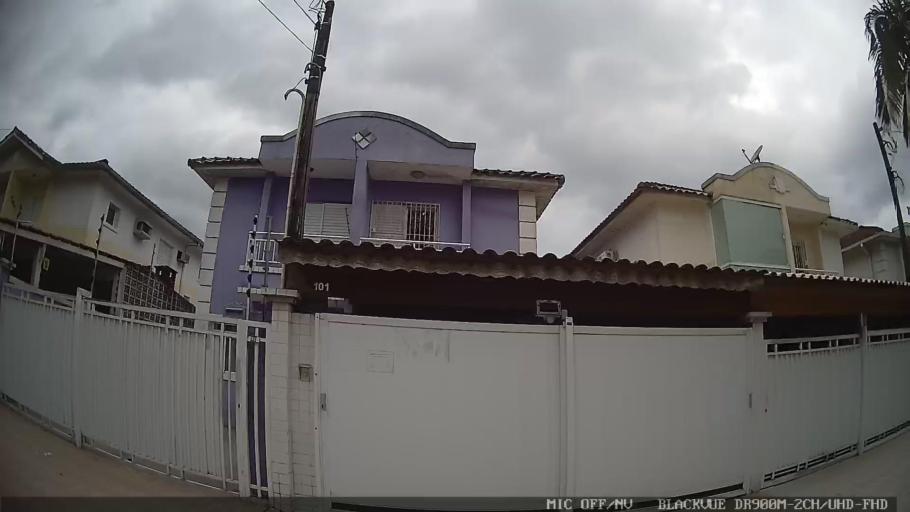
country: BR
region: Sao Paulo
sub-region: Guaruja
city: Guaruja
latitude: -23.9927
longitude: -46.2742
